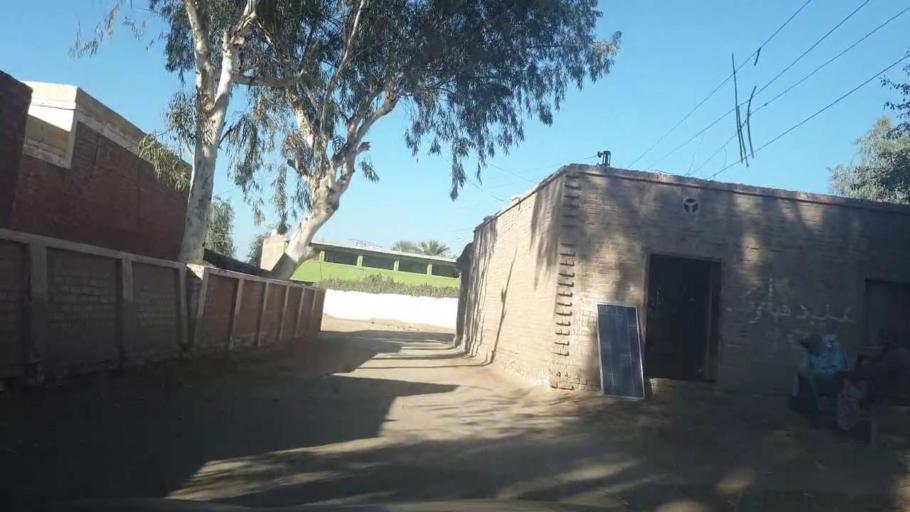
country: PK
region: Sindh
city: Adilpur
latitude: 27.9294
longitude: 69.2559
